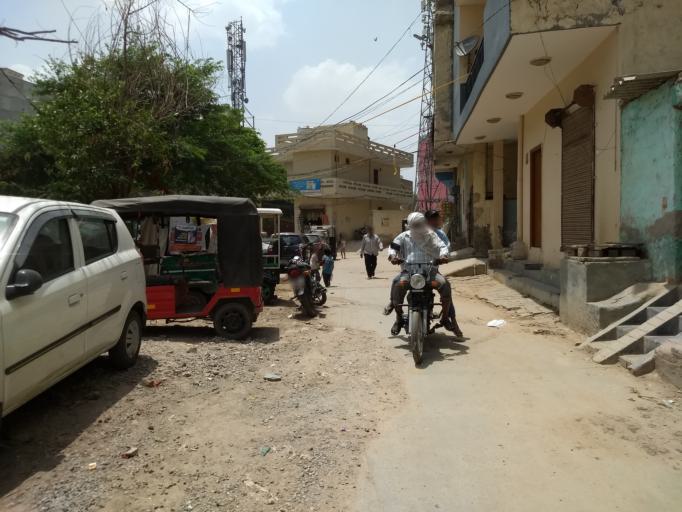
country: IN
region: Haryana
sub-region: Gurgaon
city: Gurgaon
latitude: 28.4895
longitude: 77.1024
